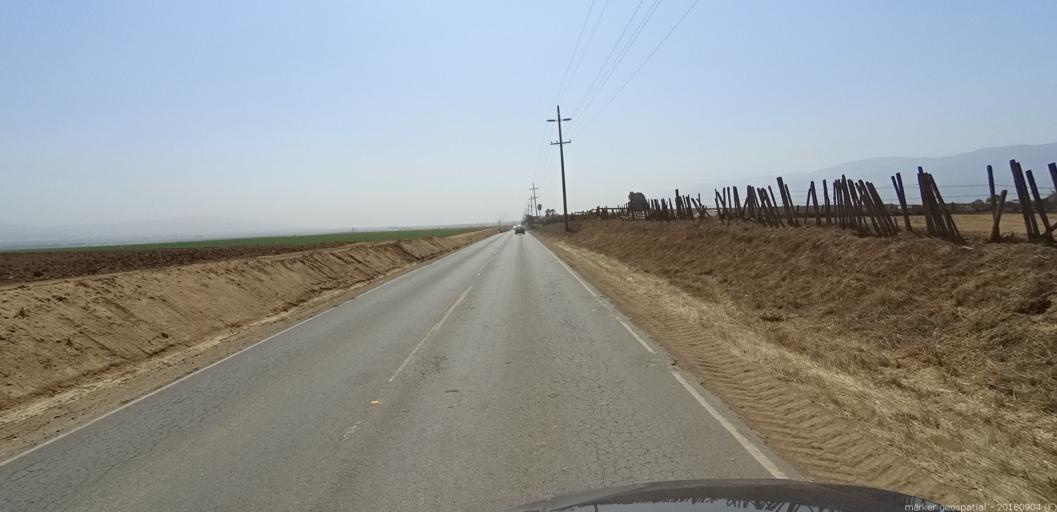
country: US
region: California
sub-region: Monterey County
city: Chualar
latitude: 36.5554
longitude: -121.4772
